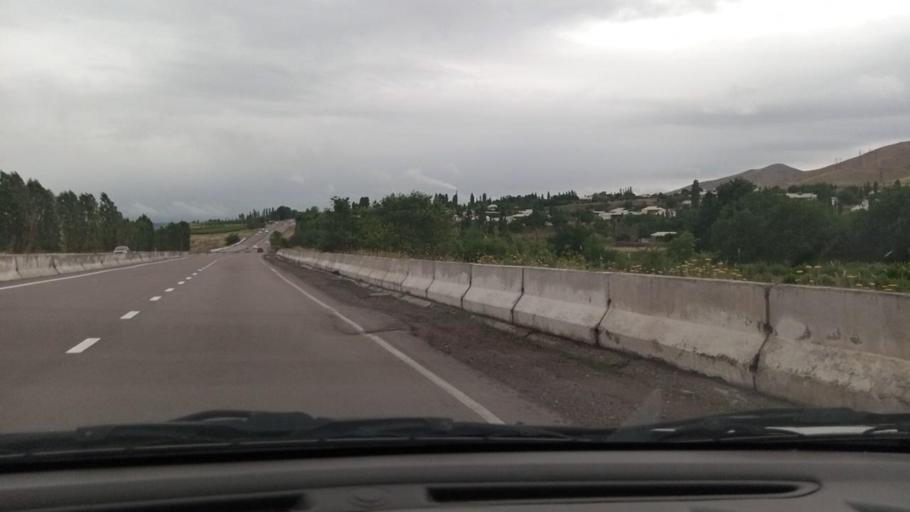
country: UZ
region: Toshkent
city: Angren
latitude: 40.9412
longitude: 69.9048
